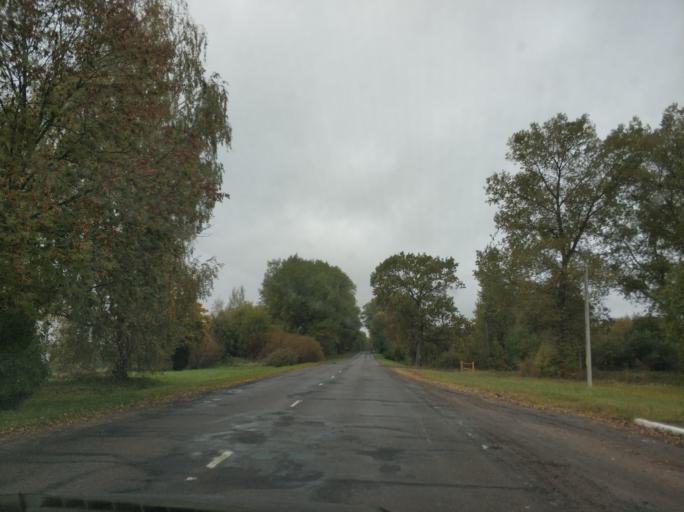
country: BY
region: Vitebsk
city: Polatsk
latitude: 55.4312
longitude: 28.9938
